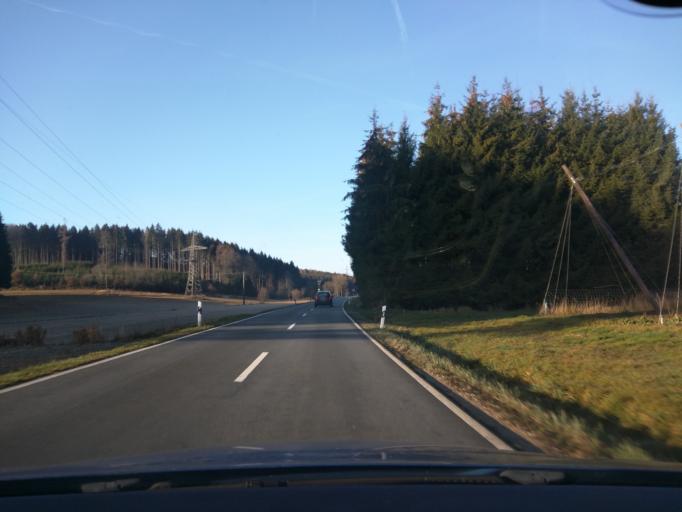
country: DE
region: Bavaria
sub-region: Upper Bavaria
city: Au in der Hallertau
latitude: 48.5667
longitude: 11.7288
